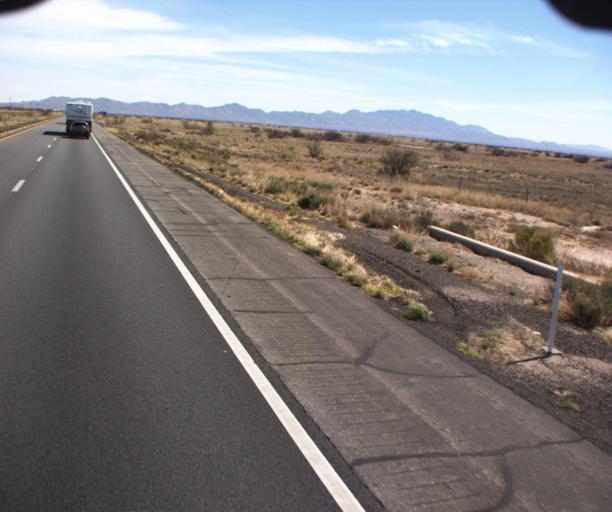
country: US
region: Arizona
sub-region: Cochise County
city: Willcox
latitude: 32.2018
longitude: -109.9065
